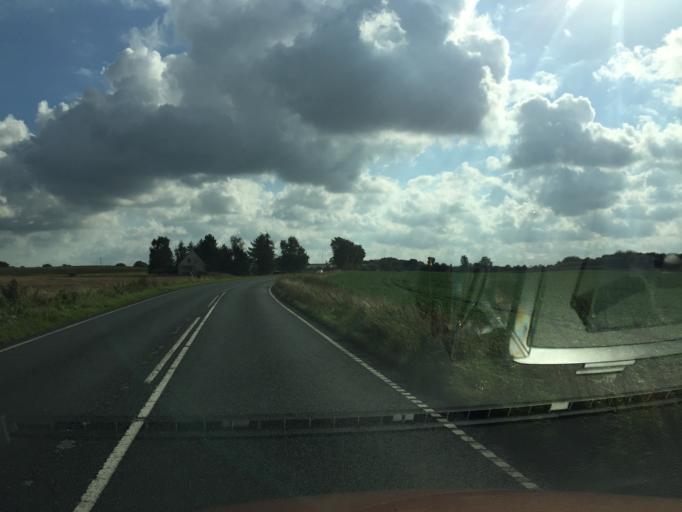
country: DK
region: South Denmark
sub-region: Sonderborg Kommune
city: Grasten
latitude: 55.0160
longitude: 9.5570
